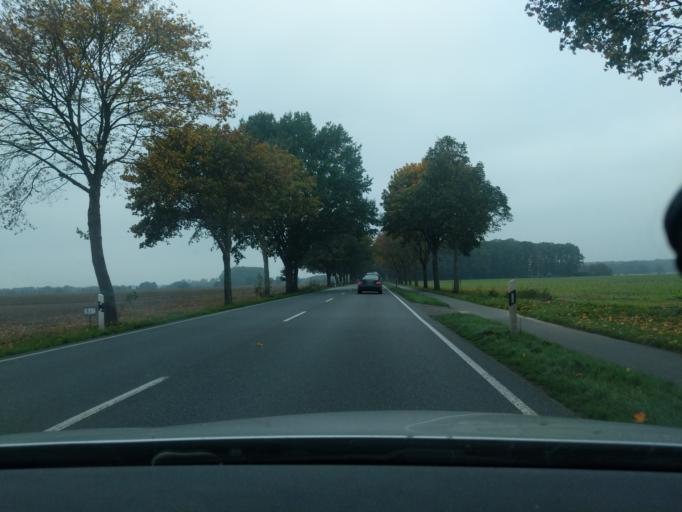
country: DE
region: Lower Saxony
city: Dudenbuttel
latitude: 53.5930
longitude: 9.3391
